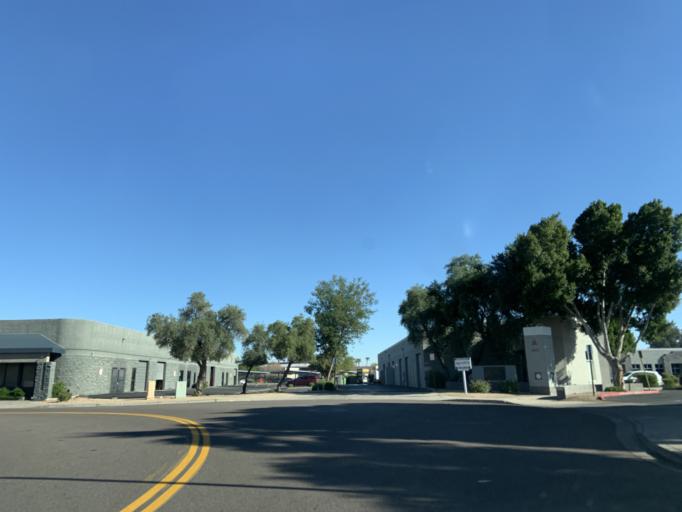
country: US
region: Arizona
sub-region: Maricopa County
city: Tempe
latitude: 33.4122
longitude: -111.8703
